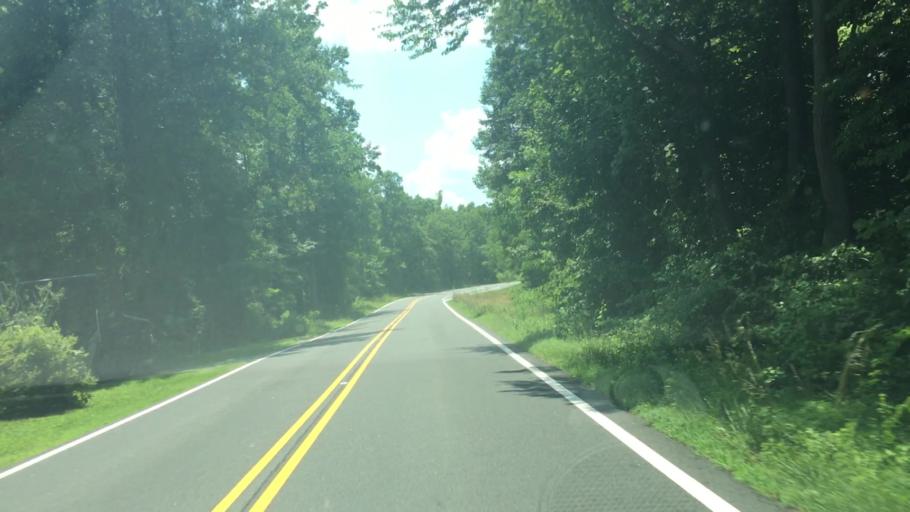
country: US
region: Virginia
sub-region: King George County
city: King George
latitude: 38.3183
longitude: -77.1881
